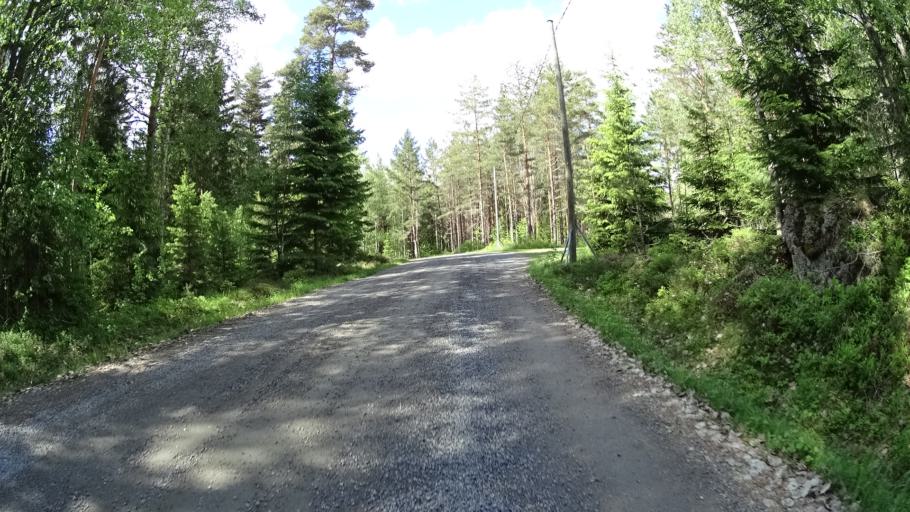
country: FI
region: Uusimaa
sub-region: Raaseporin
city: Pohja
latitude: 60.1821
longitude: 23.5848
